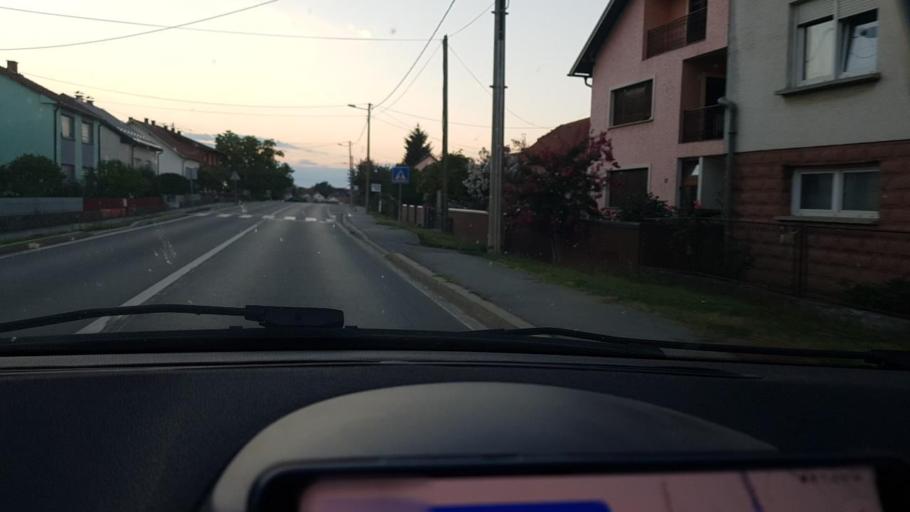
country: HR
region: Bjelovarsko-Bilogorska
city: Zdralovi
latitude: 45.8840
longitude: 16.8657
